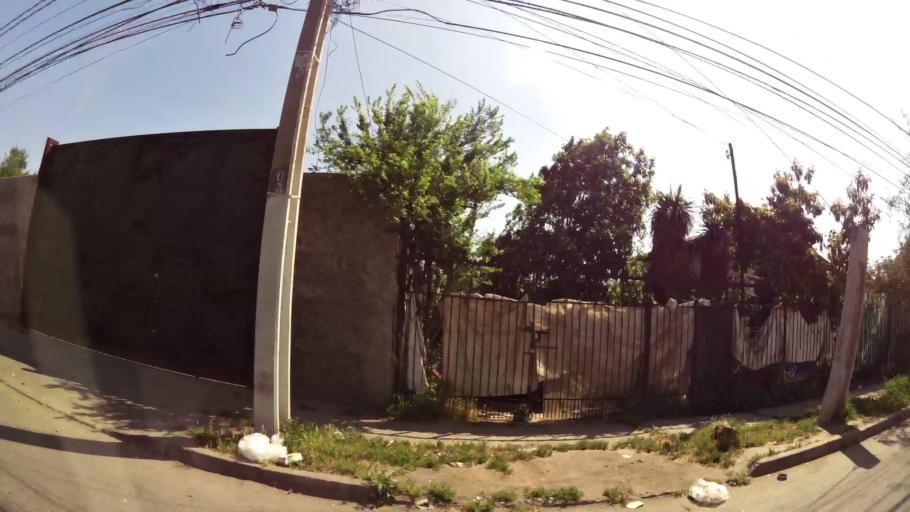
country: CL
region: Santiago Metropolitan
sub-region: Provincia de Santiago
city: La Pintana
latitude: -33.5477
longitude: -70.6100
